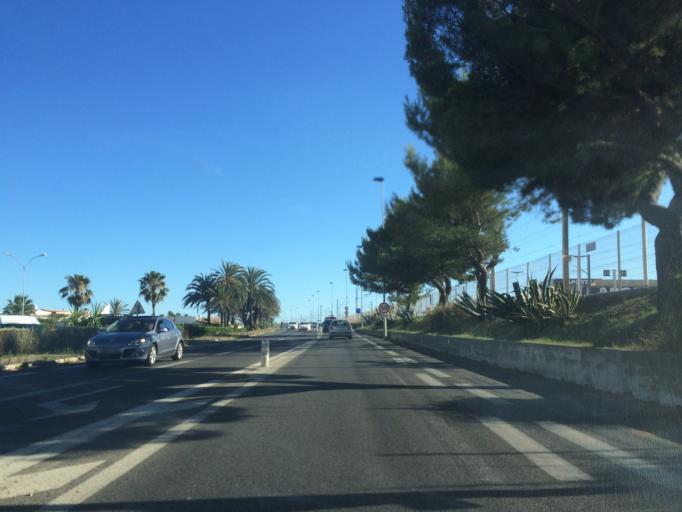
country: FR
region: Provence-Alpes-Cote d'Azur
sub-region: Departement des Alpes-Maritimes
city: Biot
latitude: 43.6104
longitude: 7.1264
